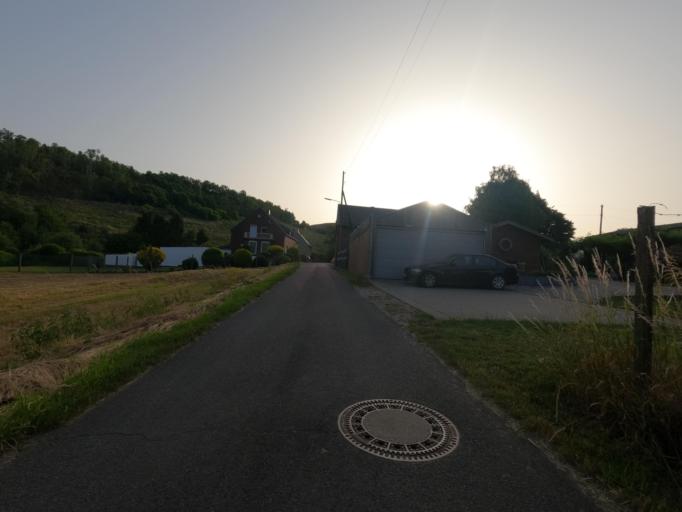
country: DE
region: North Rhine-Westphalia
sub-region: Regierungsbezirk Koln
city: Wassenberg
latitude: 51.0761
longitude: 6.1895
